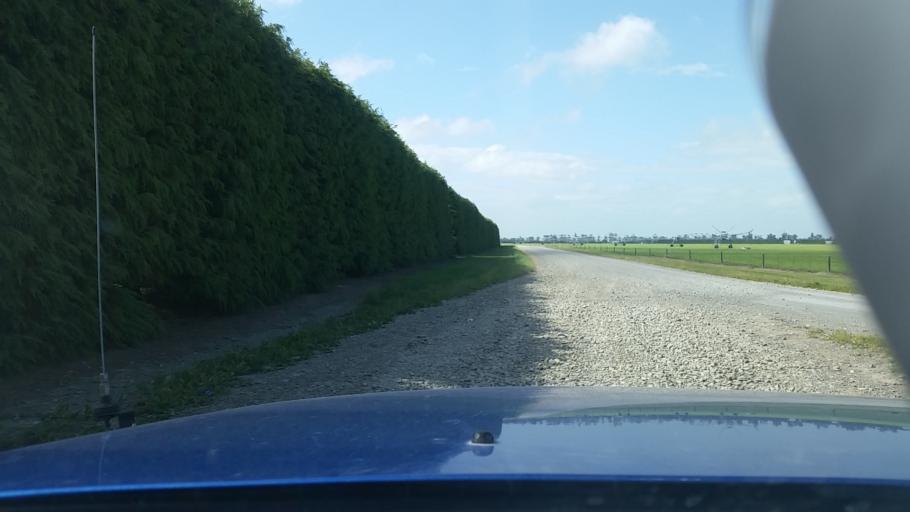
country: NZ
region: Canterbury
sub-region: Ashburton District
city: Ashburton
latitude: -43.9225
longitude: 171.9025
